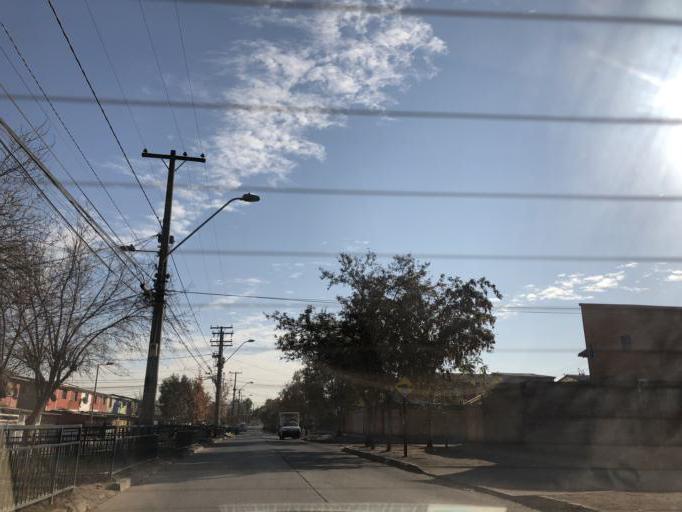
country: CL
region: Santiago Metropolitan
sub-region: Provincia de Cordillera
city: Puente Alto
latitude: -33.6230
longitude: -70.5945
